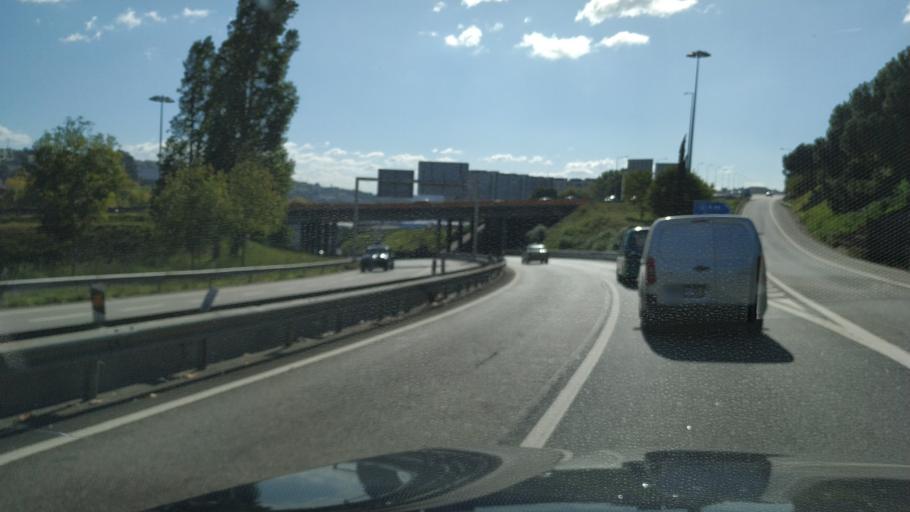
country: PT
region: Porto
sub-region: Gondomar
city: Valbom
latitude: 41.1479
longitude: -8.5815
